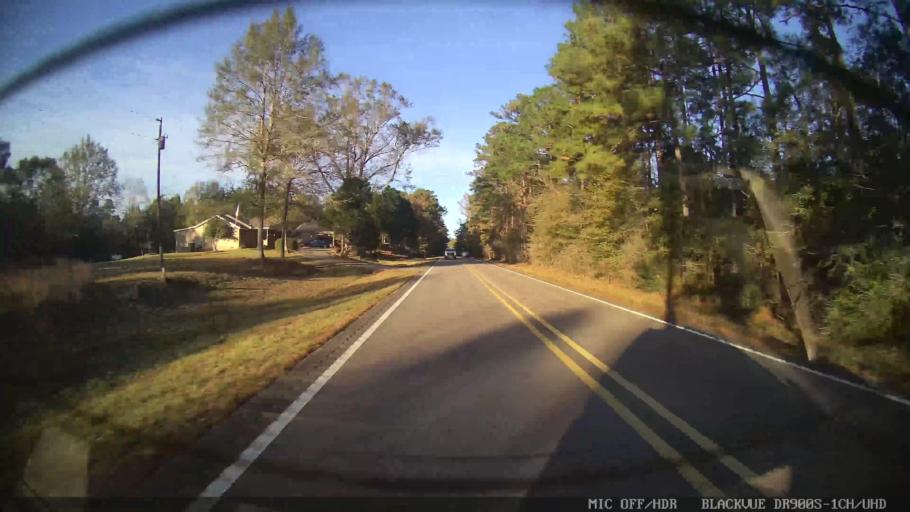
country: US
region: Mississippi
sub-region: Lamar County
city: Lumberton
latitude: 31.0570
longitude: -89.4284
